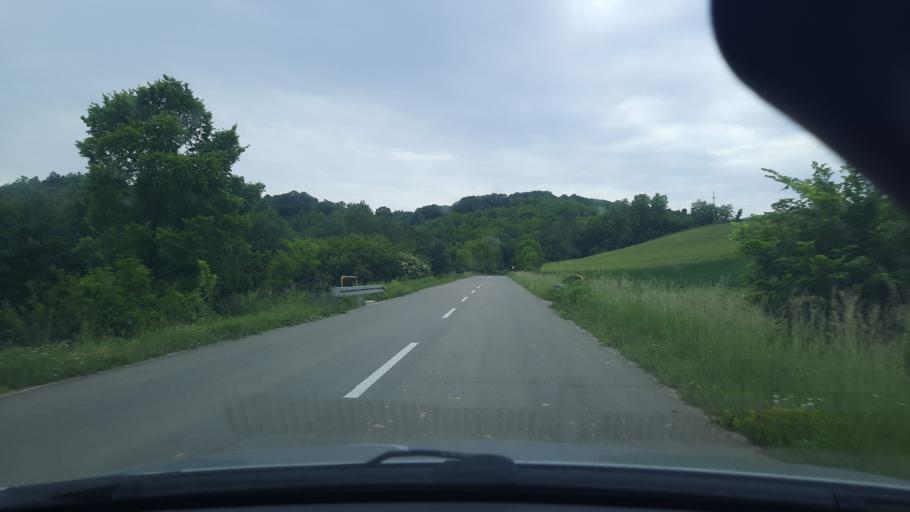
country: RS
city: Bukor
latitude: 44.5155
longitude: 19.5107
